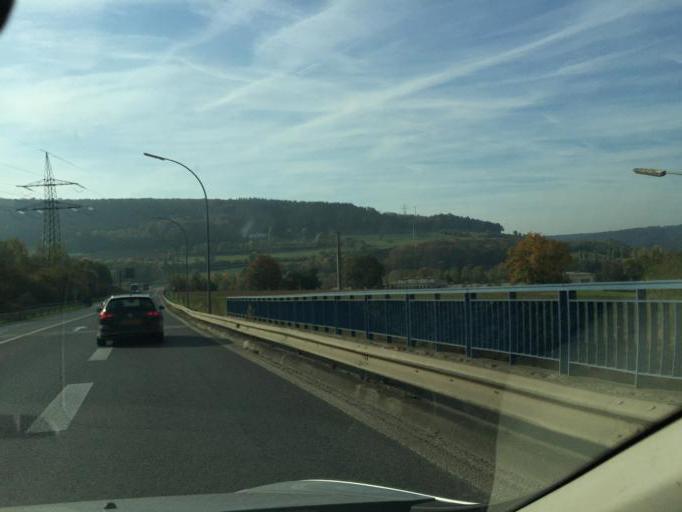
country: LU
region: Diekirch
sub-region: Canton de Diekirch
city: Erpeldange
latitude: 49.8542
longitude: 6.1218
